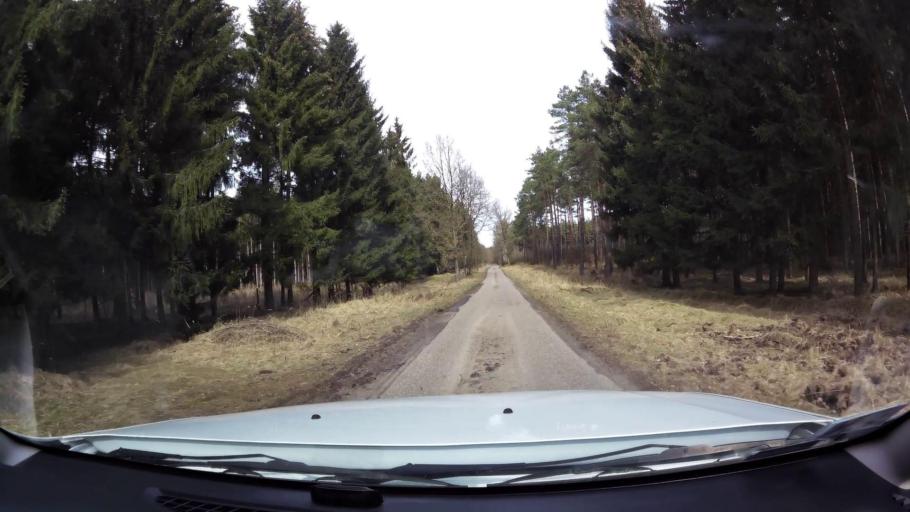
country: PL
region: West Pomeranian Voivodeship
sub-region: Powiat drawski
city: Drawsko Pomorskie
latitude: 53.4869
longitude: 15.7004
